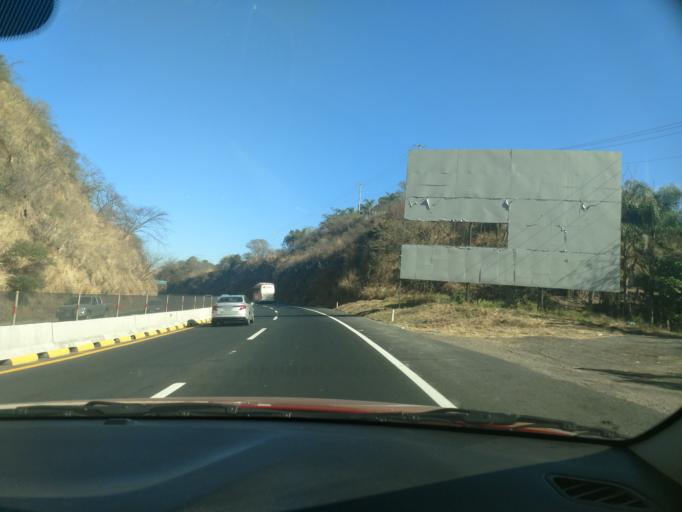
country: MX
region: Nayarit
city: Tepic
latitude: 21.5570
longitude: -104.9612
